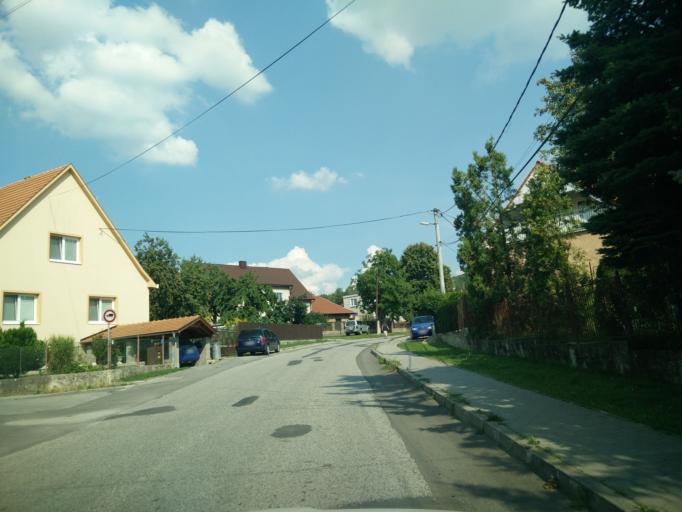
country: SK
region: Nitriansky
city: Prievidza
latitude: 48.7300
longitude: 18.6256
